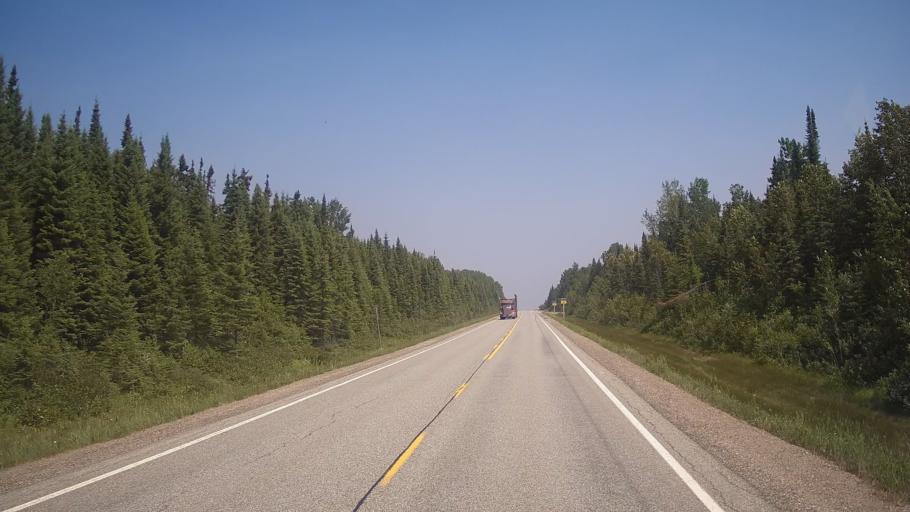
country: CA
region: Ontario
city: Timmins
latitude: 48.1987
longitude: -81.5804
